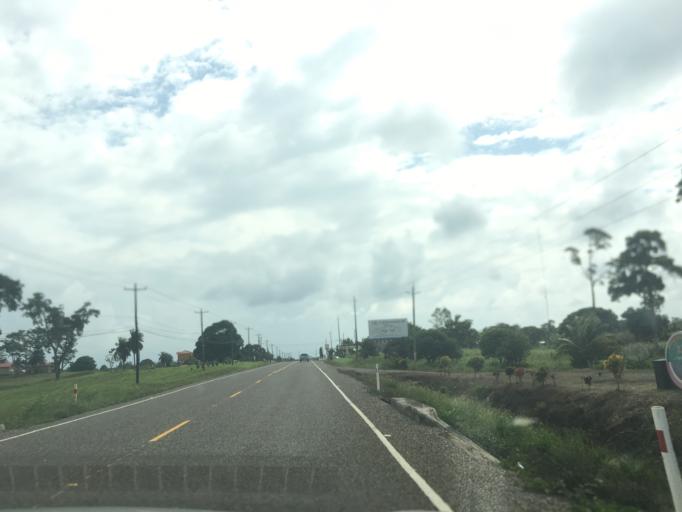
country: BZ
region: Stann Creek
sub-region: Dangriga
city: Dangriga
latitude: 16.9878
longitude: -88.2982
